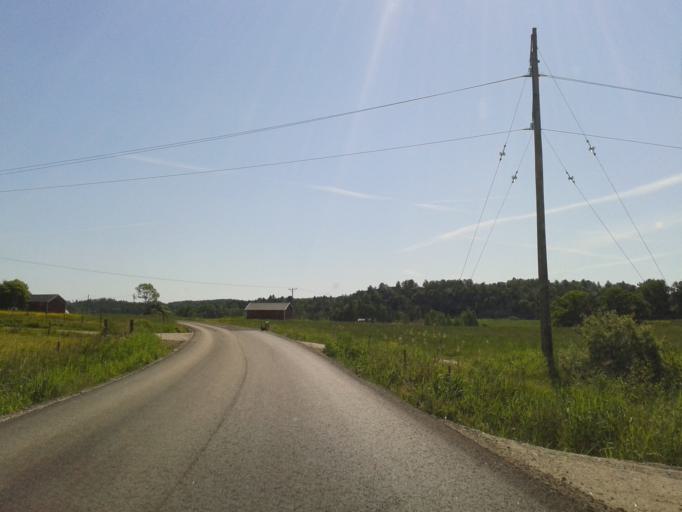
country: SE
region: Vaestra Goetaland
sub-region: Orust
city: Henan
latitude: 58.2577
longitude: 11.7366
